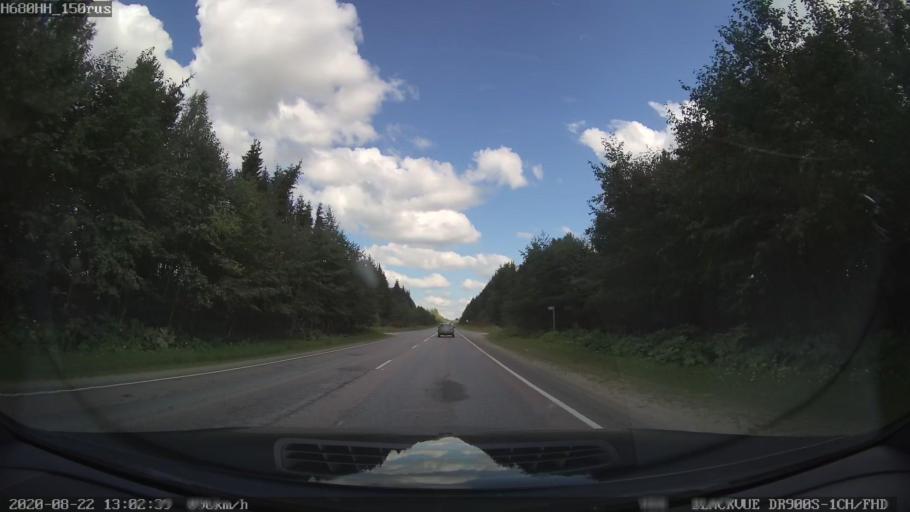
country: RU
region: Tverskaya
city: Bezhetsk
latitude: 57.6514
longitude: 36.3999
